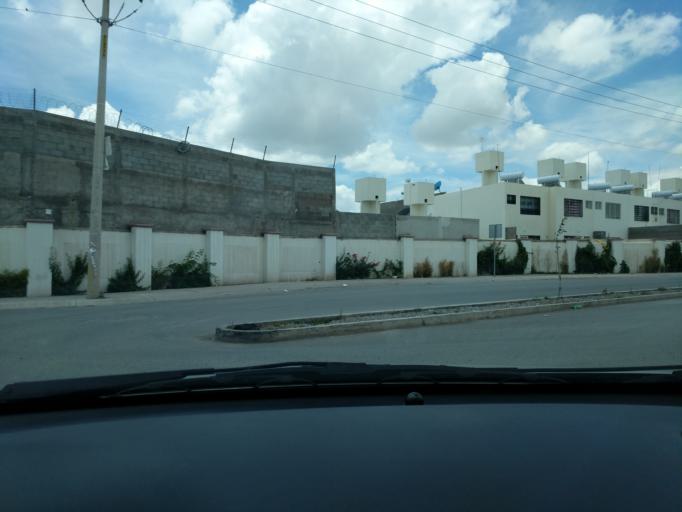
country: MX
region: San Luis Potosi
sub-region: San Luis Potosi
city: Fraccion Milpillas
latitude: 22.2217
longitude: -100.9339
